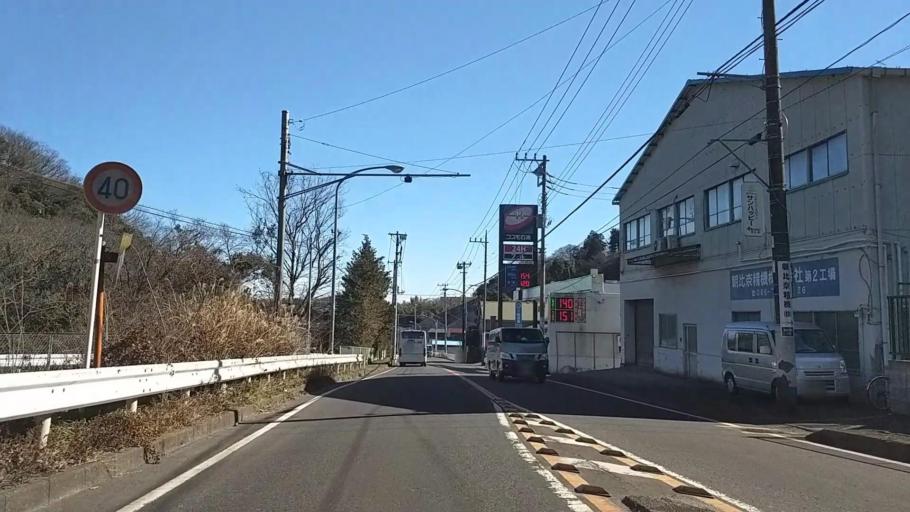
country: JP
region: Kanagawa
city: Zushi
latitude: 35.3301
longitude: 139.5947
